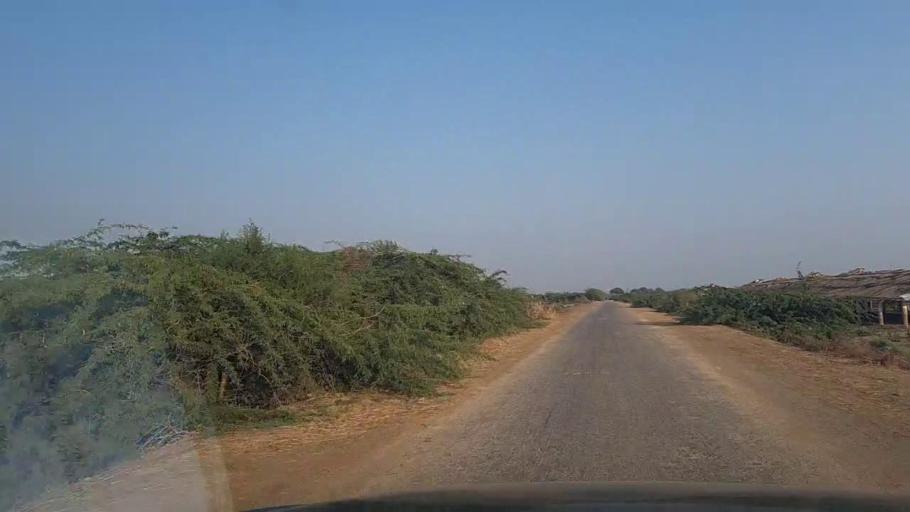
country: PK
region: Sindh
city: Keti Bandar
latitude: 24.2657
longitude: 67.5617
